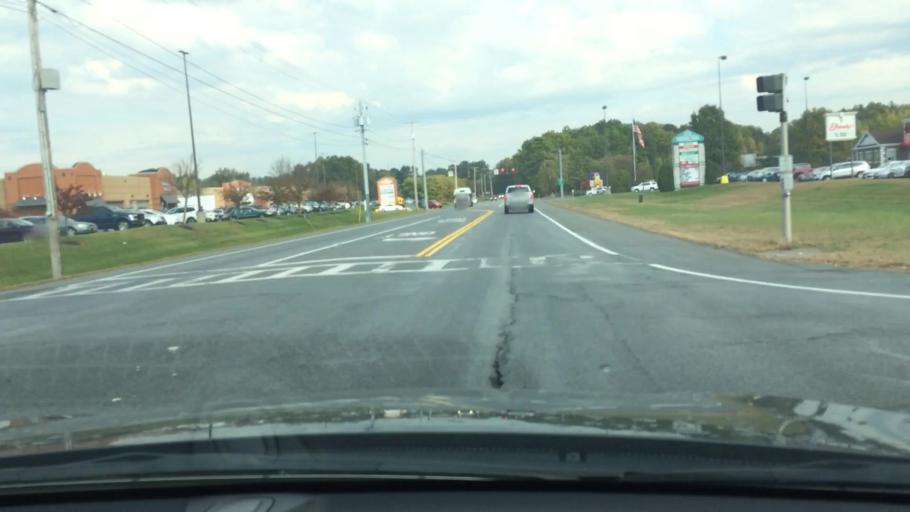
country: US
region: New York
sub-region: Saratoga County
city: Saratoga Springs
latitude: 43.1055
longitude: -73.7406
